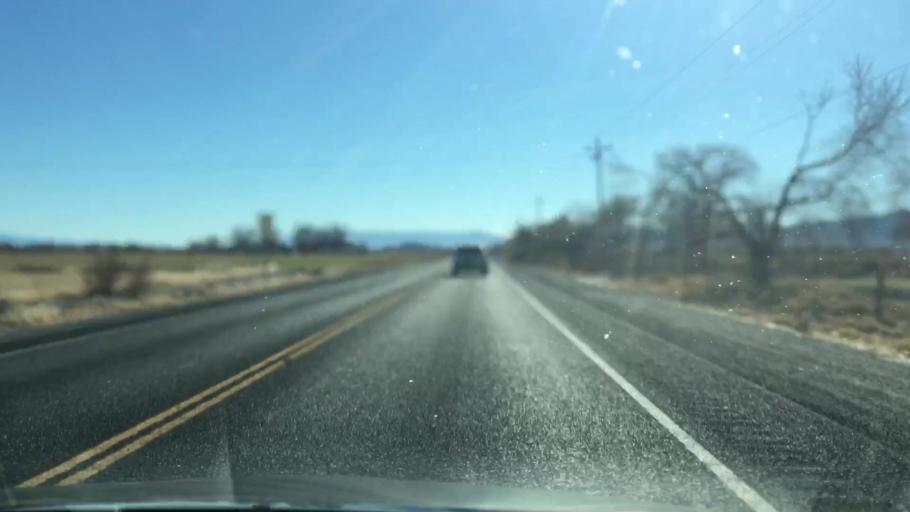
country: US
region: Nevada
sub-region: Lyon County
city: Yerington
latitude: 39.0671
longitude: -119.1813
